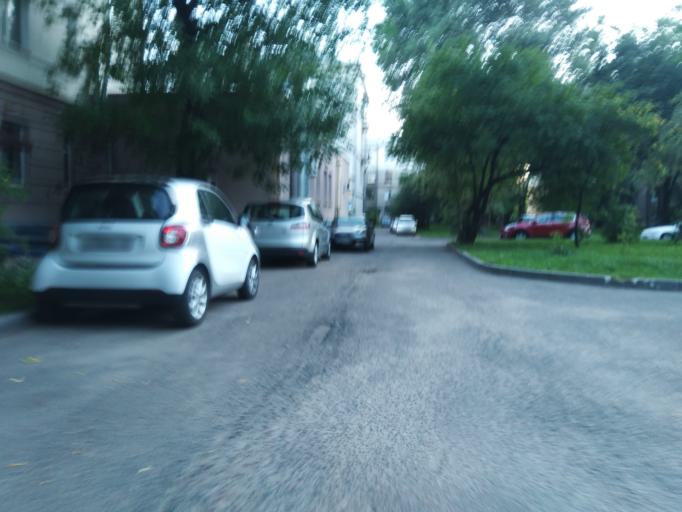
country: BY
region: Minsk
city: Minsk
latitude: 53.8944
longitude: 27.5756
